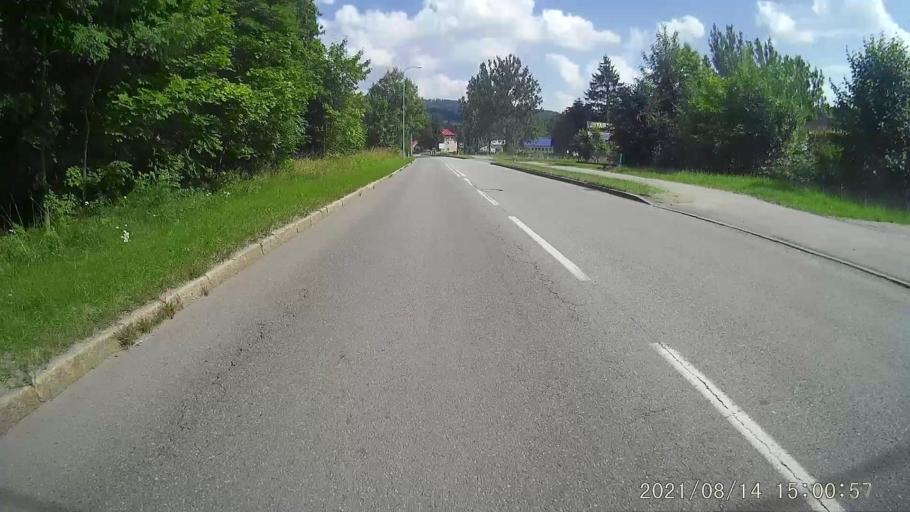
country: PL
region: Lower Silesian Voivodeship
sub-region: Powiat walbrzyski
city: Jedlina-Zdroj
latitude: 50.7167
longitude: 16.3510
